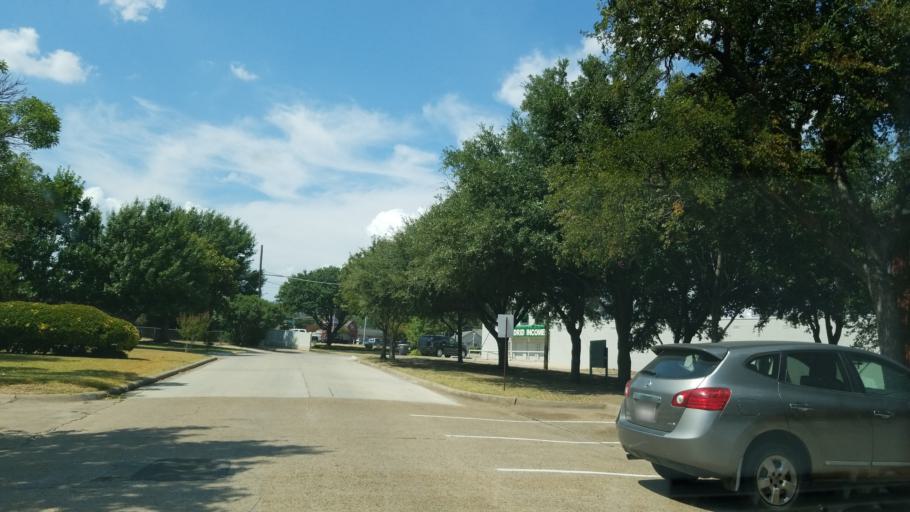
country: US
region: Texas
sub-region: Dallas County
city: Cockrell Hill
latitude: 32.7622
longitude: -96.8546
